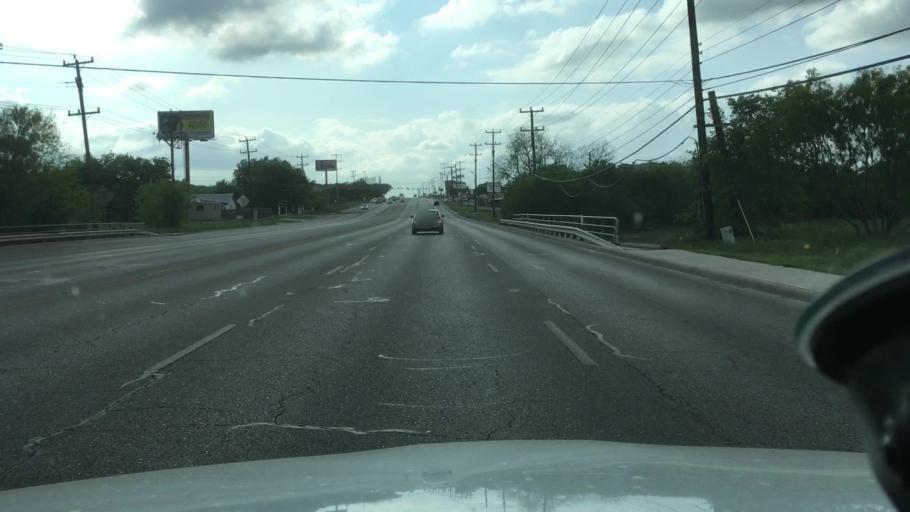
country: US
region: Texas
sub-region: Bexar County
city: Windcrest
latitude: 29.5003
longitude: -98.3538
